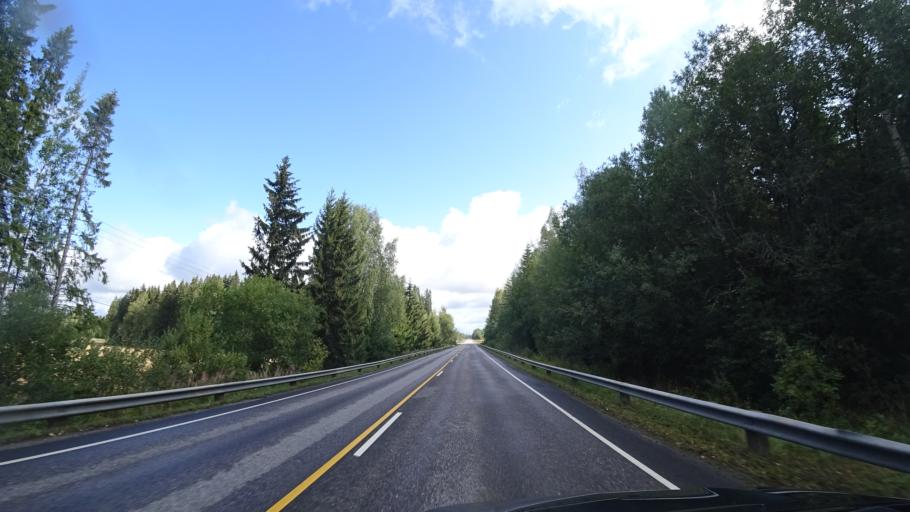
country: FI
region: Uusimaa
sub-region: Helsinki
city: Hyvinge
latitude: 60.5388
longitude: 24.9256
